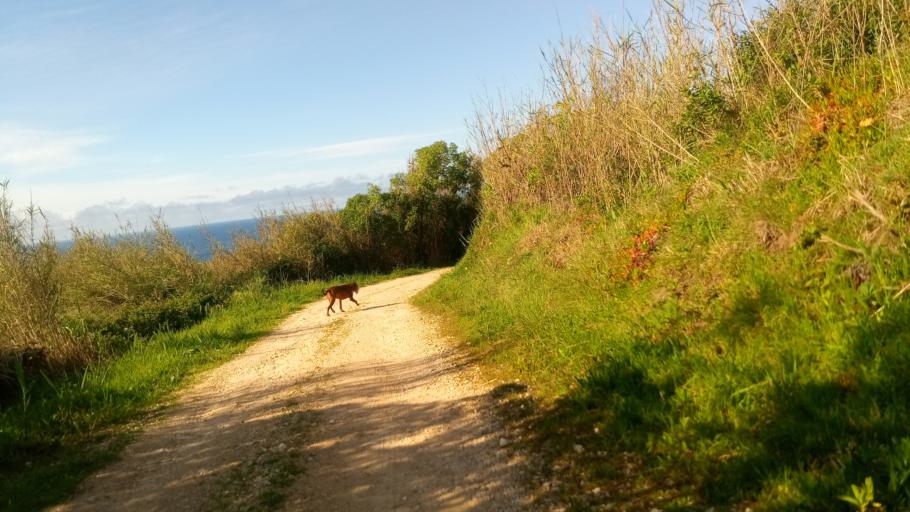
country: PT
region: Leiria
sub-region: Caldas da Rainha
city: Caldas da Rainha
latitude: 39.4918
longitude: -9.1752
